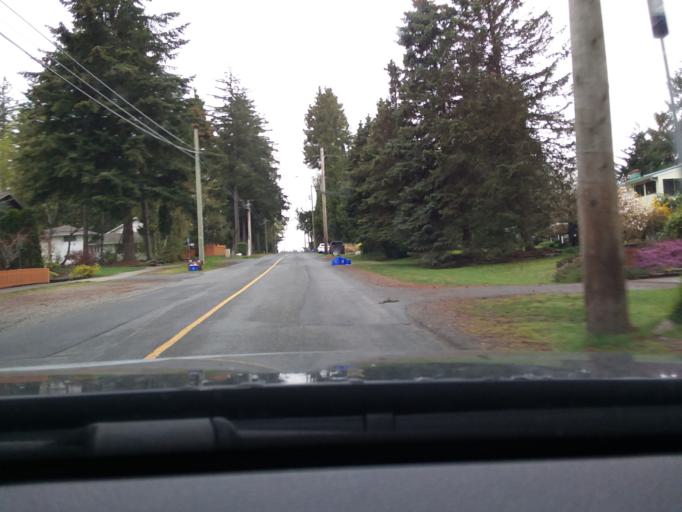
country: CA
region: British Columbia
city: North Saanich
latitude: 48.5544
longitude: -123.3982
